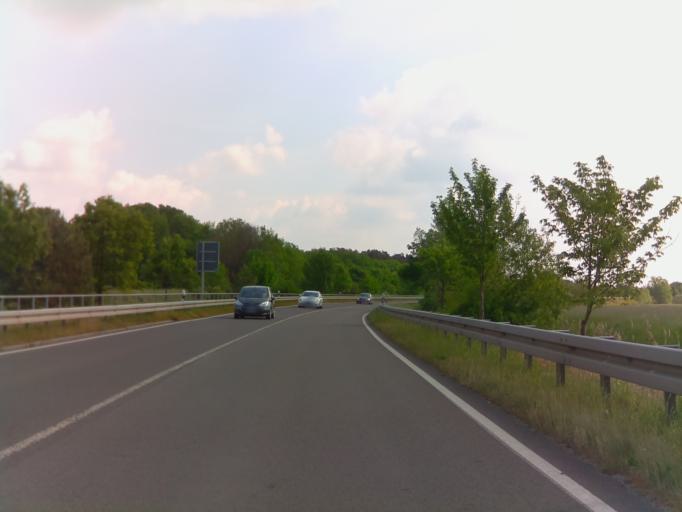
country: DE
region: Saxony-Anhalt
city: Uenglingen
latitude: 52.5730
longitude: 11.7935
